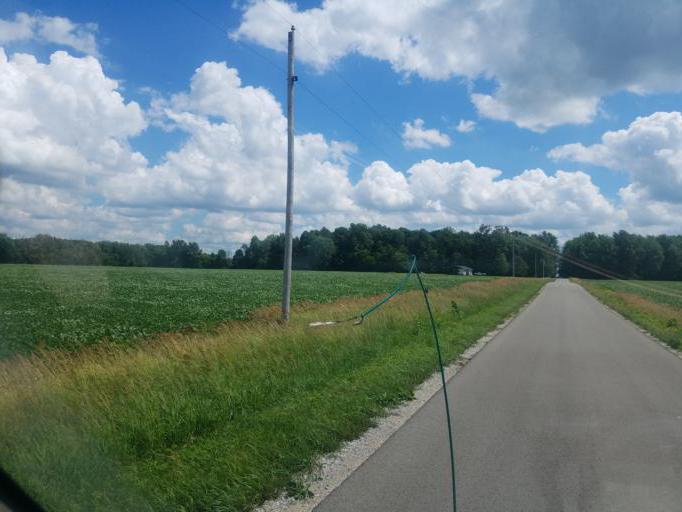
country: US
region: Ohio
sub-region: Crawford County
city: Galion
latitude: 40.8096
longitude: -82.8381
